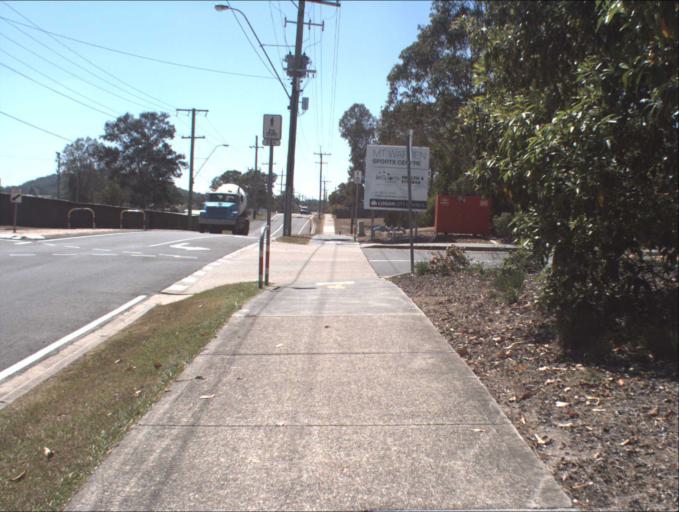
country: AU
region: Queensland
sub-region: Logan
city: Windaroo
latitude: -27.7220
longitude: 153.1964
